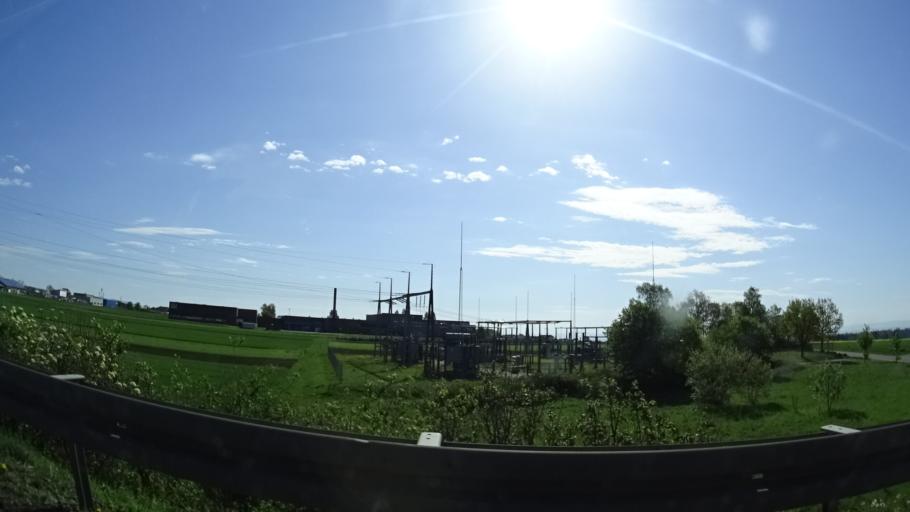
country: DE
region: Baden-Wuerttemberg
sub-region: Regierungsbezirk Stuttgart
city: Motzingen
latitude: 48.5339
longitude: 8.7611
